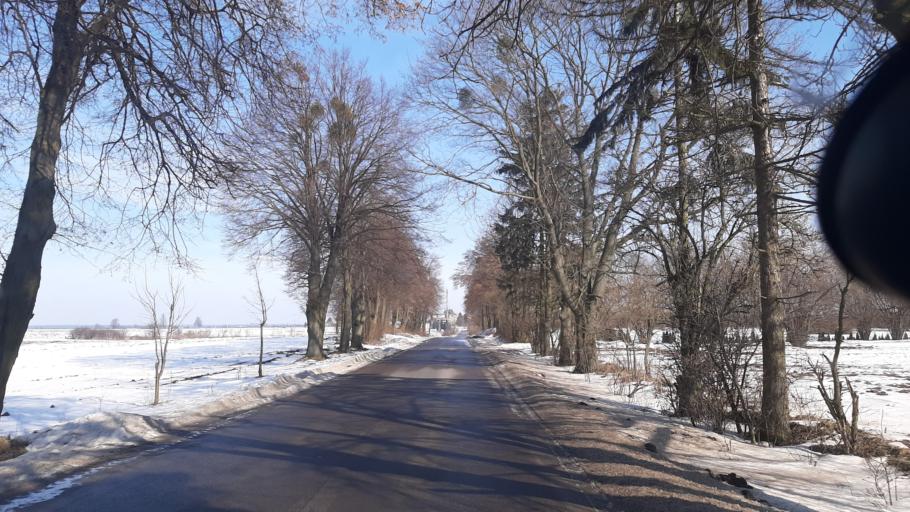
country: PL
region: Lublin Voivodeship
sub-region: Powiat pulawski
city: Kurow
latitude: 51.3809
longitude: 22.1608
